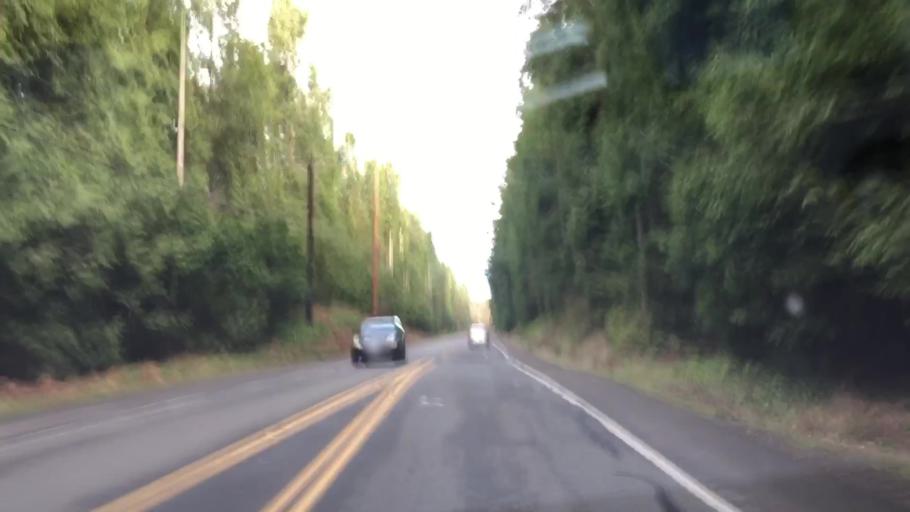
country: US
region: Washington
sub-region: Kitsap County
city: Suquamish
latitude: 47.7161
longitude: -122.5707
